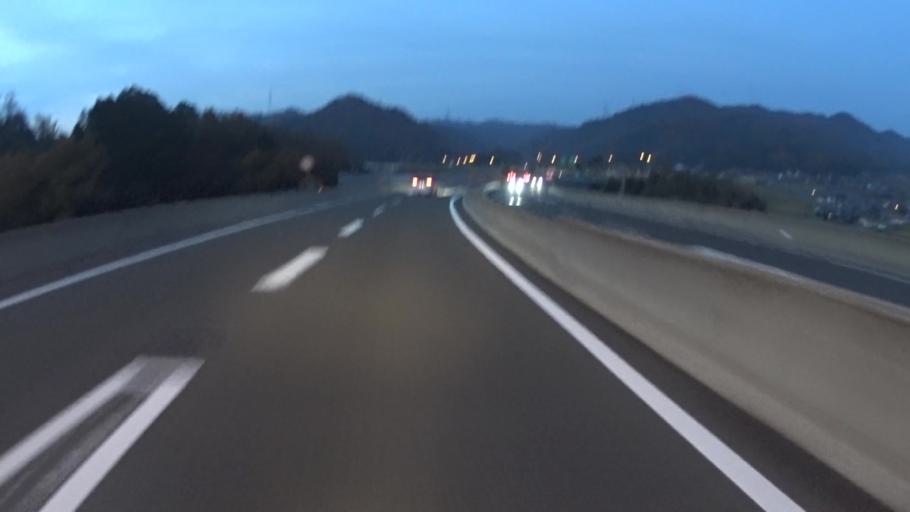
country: JP
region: Kyoto
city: Ayabe
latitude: 35.3508
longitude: 135.2907
